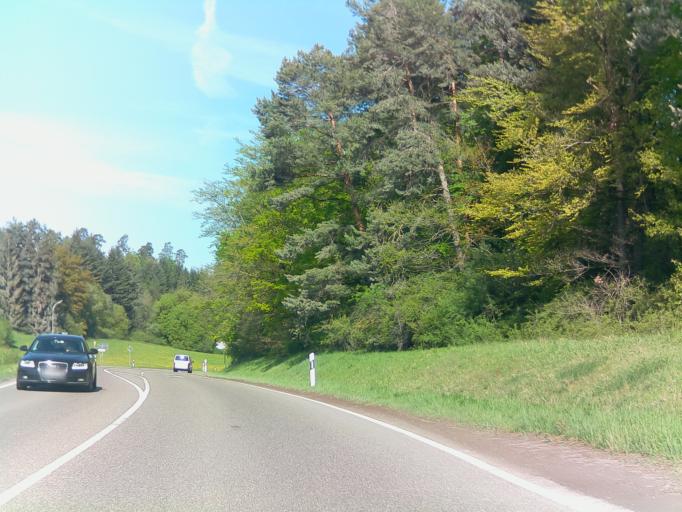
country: DE
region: Baden-Wuerttemberg
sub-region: Regierungsbezirk Stuttgart
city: Motzingen
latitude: 48.5424
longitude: 8.7567
